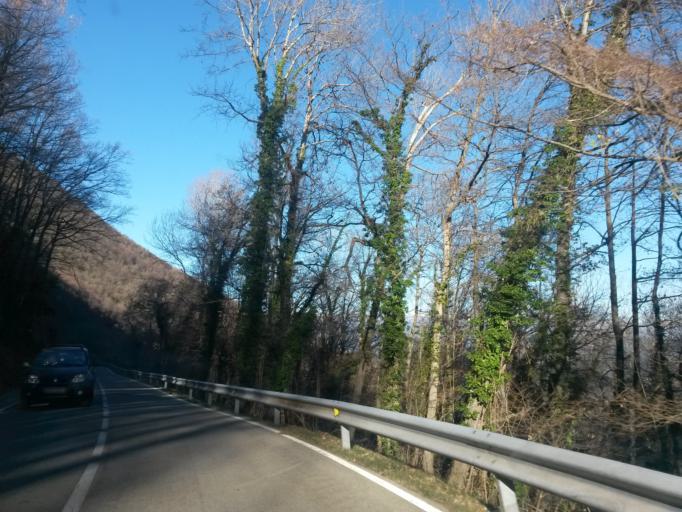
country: ES
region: Catalonia
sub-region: Provincia de Girona
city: Sant Feliu de Pallerols
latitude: 42.0653
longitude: 2.4993
